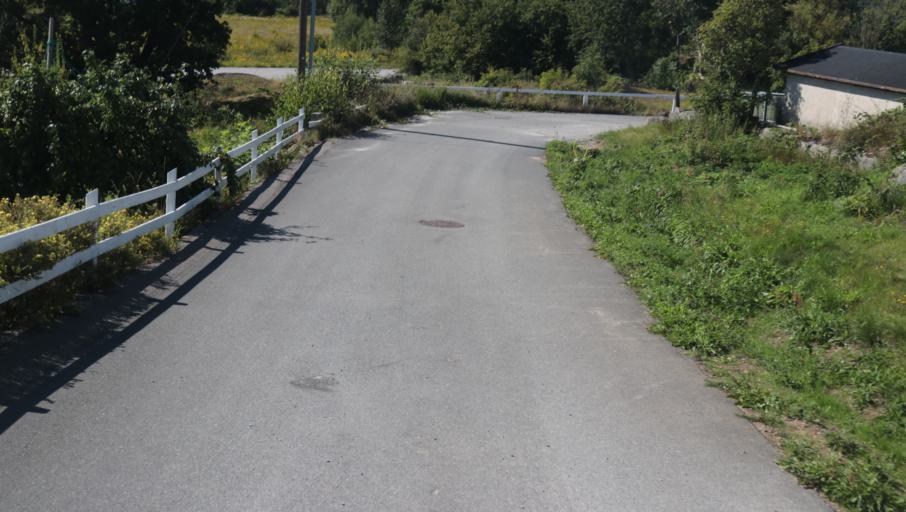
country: SE
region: Blekinge
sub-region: Karlshamns Kommun
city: Karlshamn
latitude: 56.1592
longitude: 14.8547
